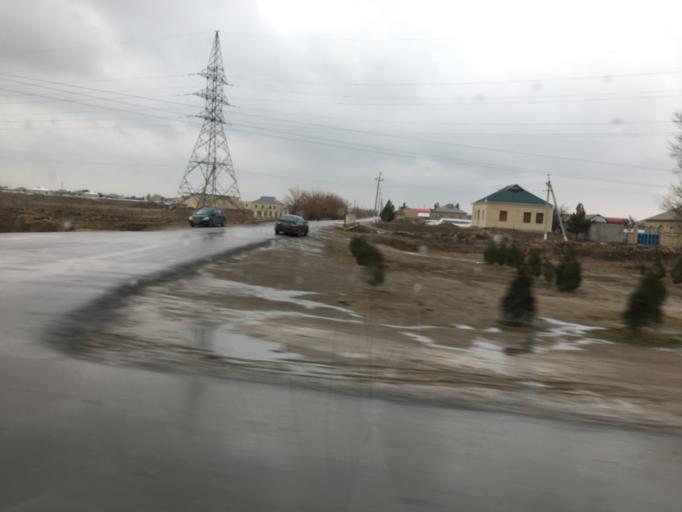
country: TM
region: Mary
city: Mary
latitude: 37.5372
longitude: 61.8828
